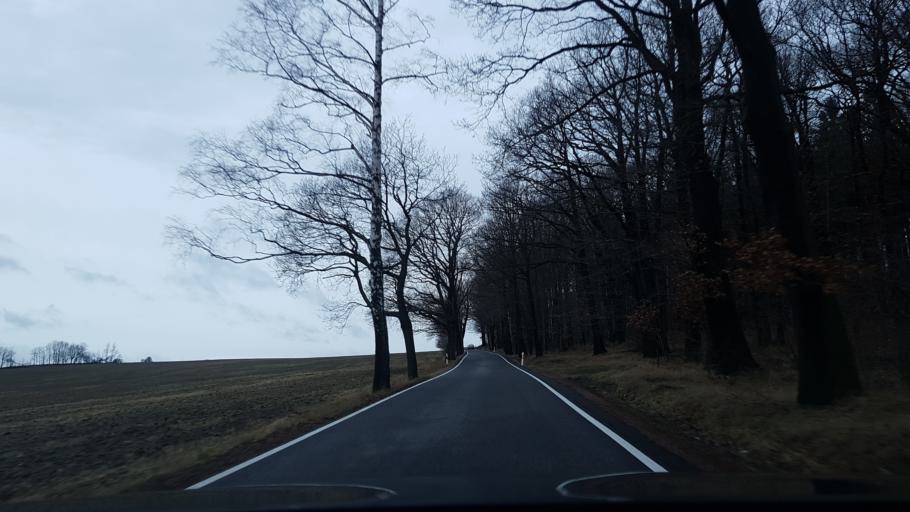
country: DE
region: Saxony
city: Liebstadt
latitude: 50.8309
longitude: 13.8987
